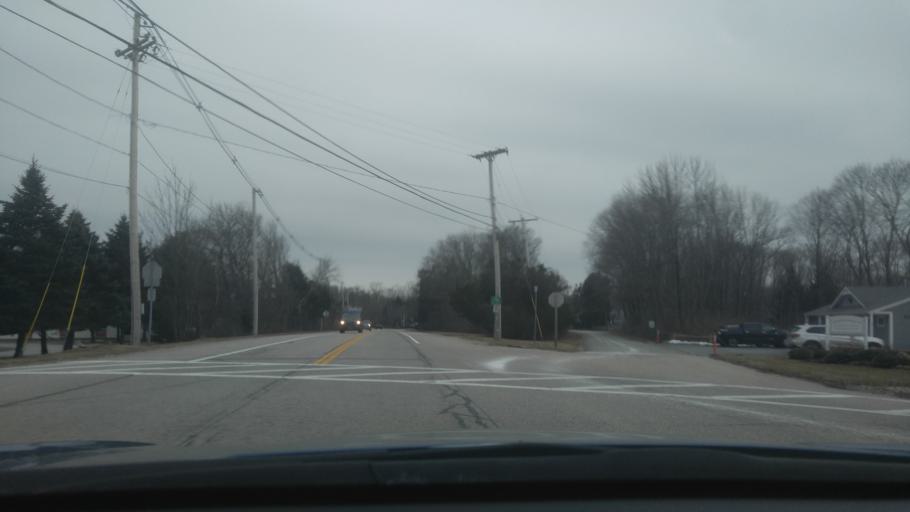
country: US
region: Rhode Island
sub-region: Washington County
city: North Kingstown
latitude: 41.5486
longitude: -71.4413
